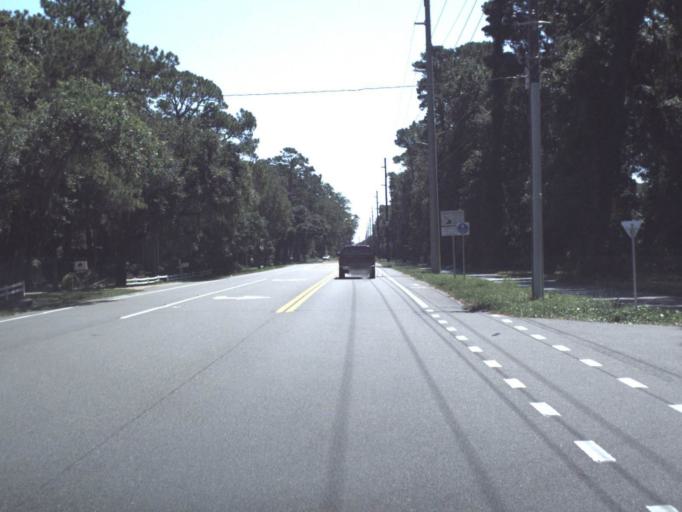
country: US
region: Florida
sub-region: Nassau County
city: Fernandina Beach
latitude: 30.5936
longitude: -81.4567
